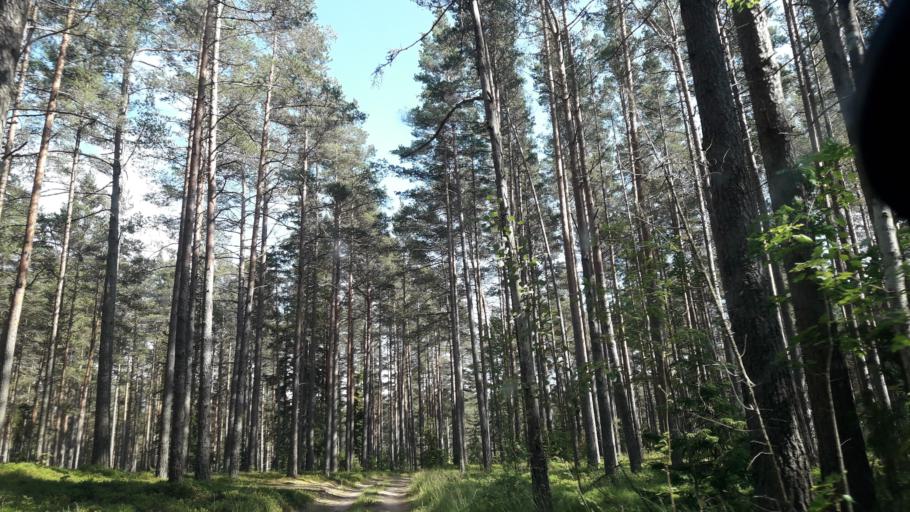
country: LV
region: Ventspils
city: Ventspils
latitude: 57.5166
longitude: 21.8790
